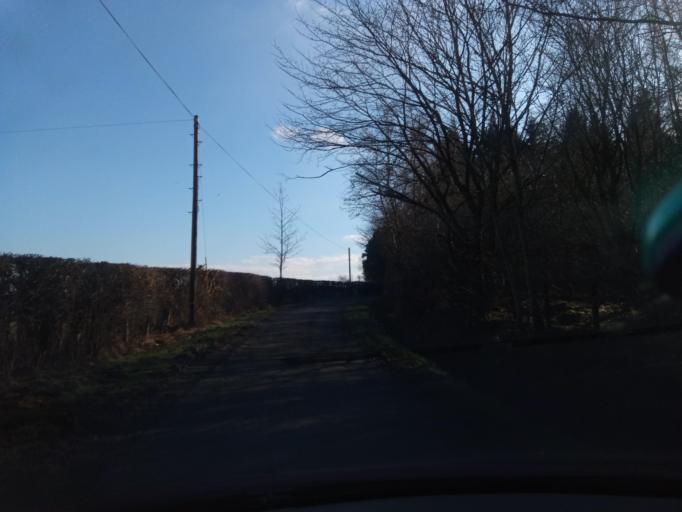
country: GB
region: Scotland
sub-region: The Scottish Borders
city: Hawick
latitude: 55.4957
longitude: -2.7872
